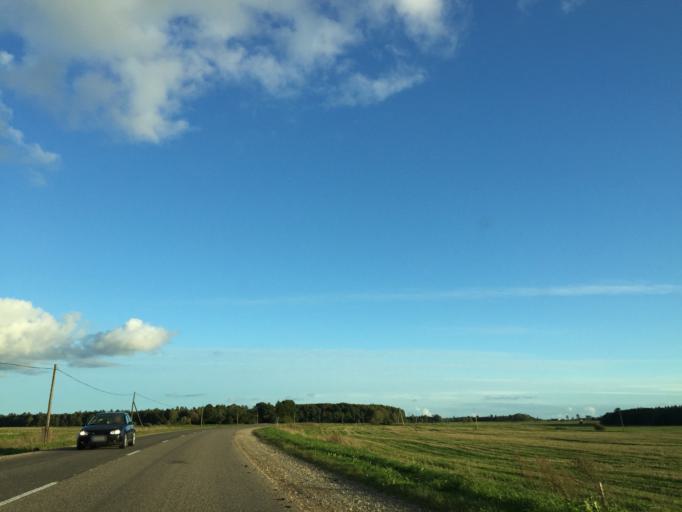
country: LV
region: Saldus Rajons
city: Saldus
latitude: 56.7480
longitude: 22.3755
